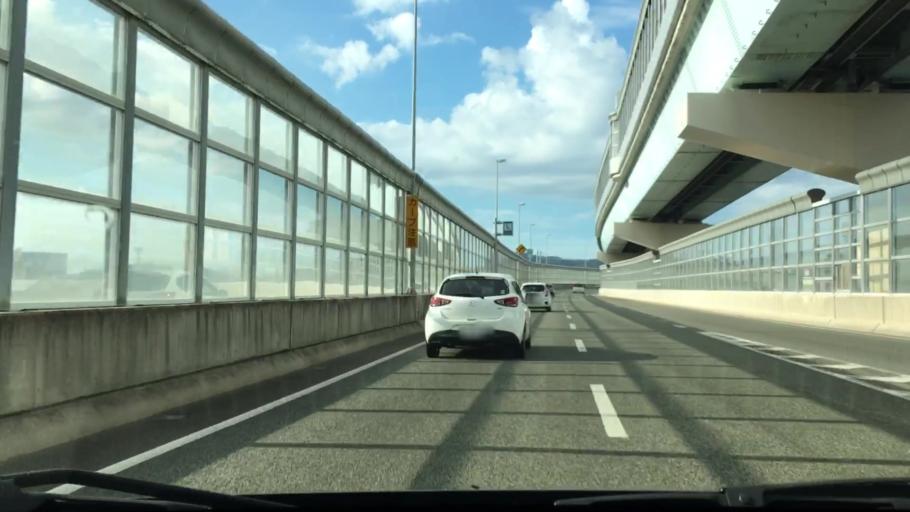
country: JP
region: Fukuoka
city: Fukuoka-shi
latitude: 33.5747
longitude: 130.3161
